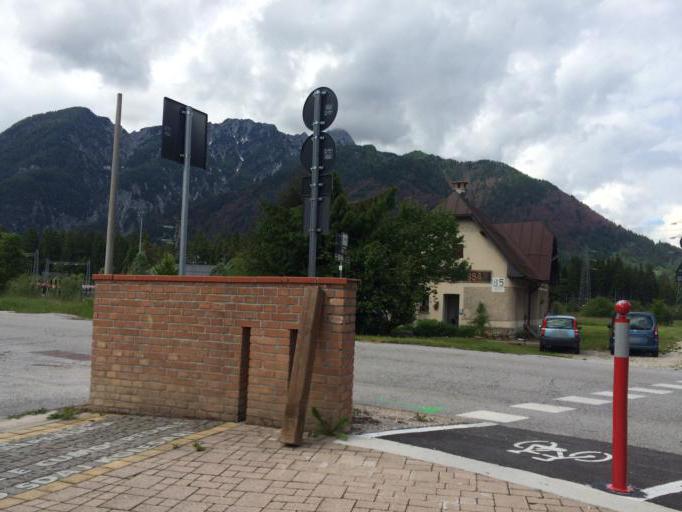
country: IT
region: Friuli Venezia Giulia
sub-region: Provincia di Udine
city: Malborghetto
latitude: 46.5011
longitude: 13.5015
